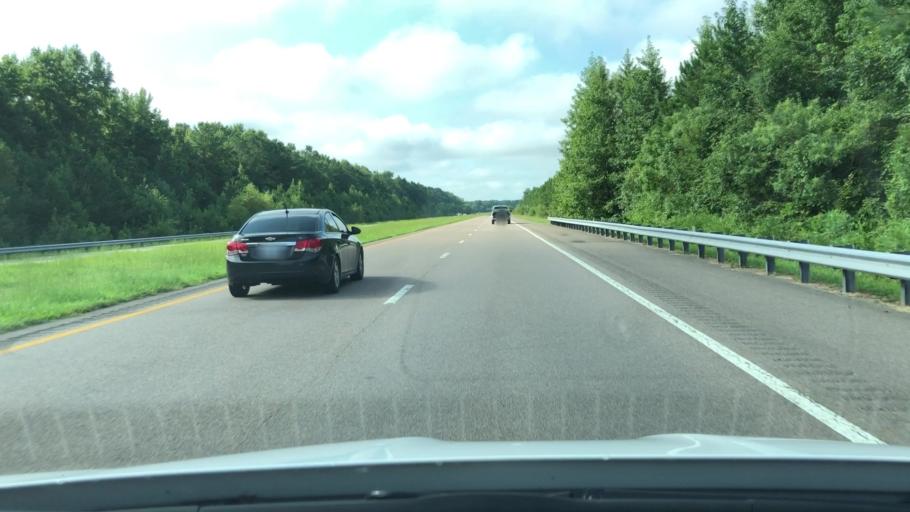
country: US
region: Virginia
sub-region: City of Portsmouth
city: Portsmouth Heights
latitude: 36.6650
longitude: -76.3550
